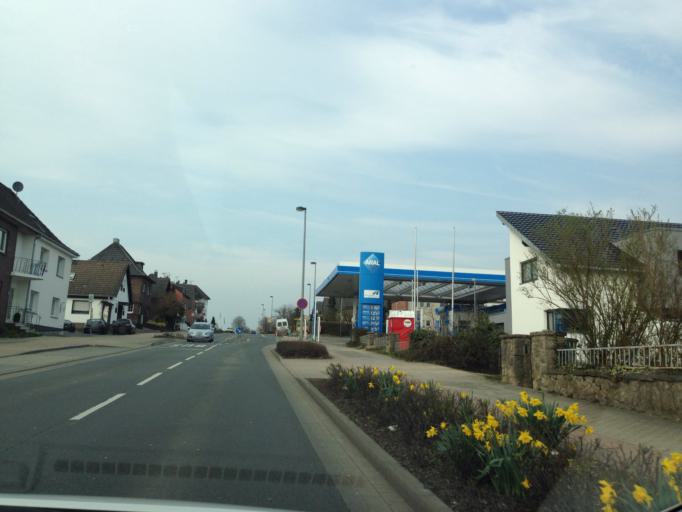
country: DE
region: North Rhine-Westphalia
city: Erkelenz
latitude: 51.0395
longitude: 6.2817
